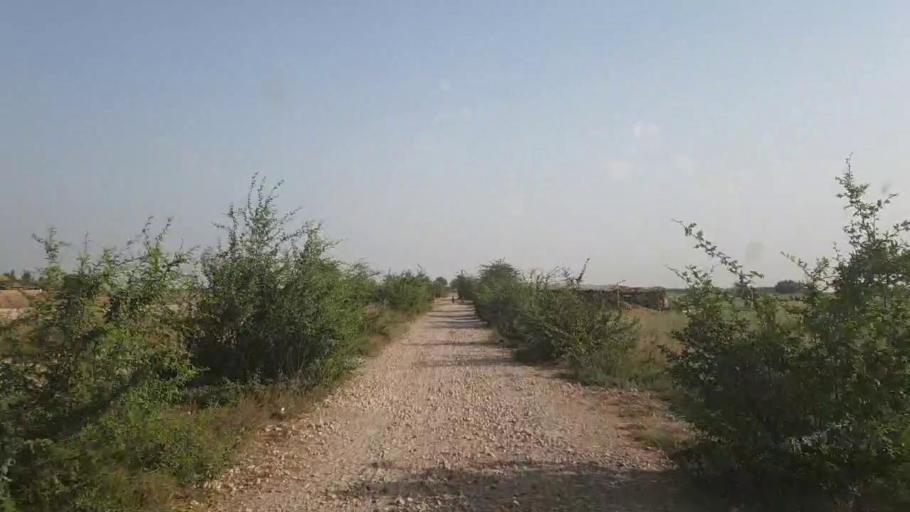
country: PK
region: Sindh
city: Kario
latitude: 24.5955
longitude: 68.5543
